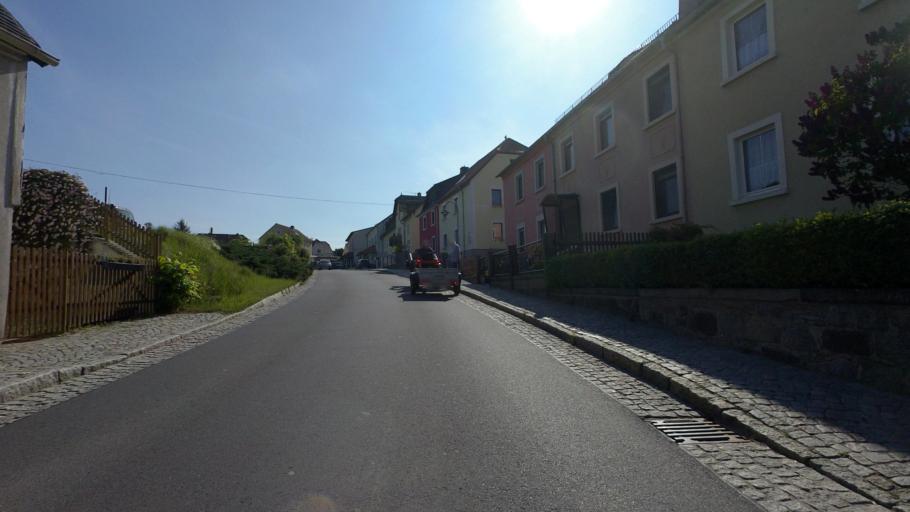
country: DE
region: Saxony
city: Elstra
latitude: 51.2229
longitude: 14.1298
